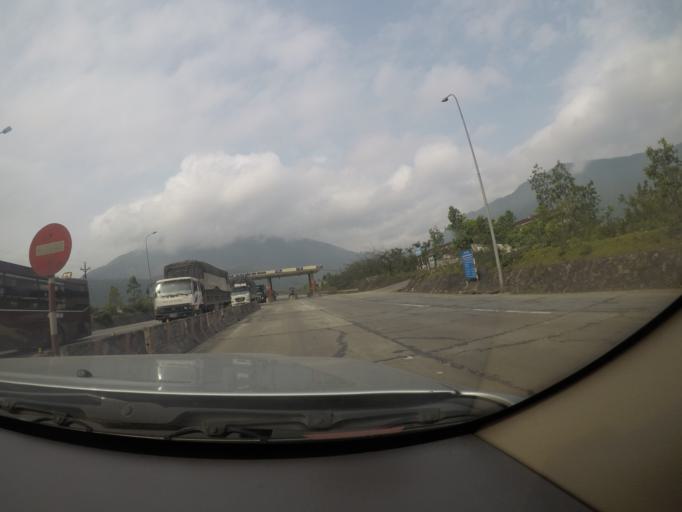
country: VN
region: Ha Tinh
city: Ky Anh
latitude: 17.9668
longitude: 106.4701
